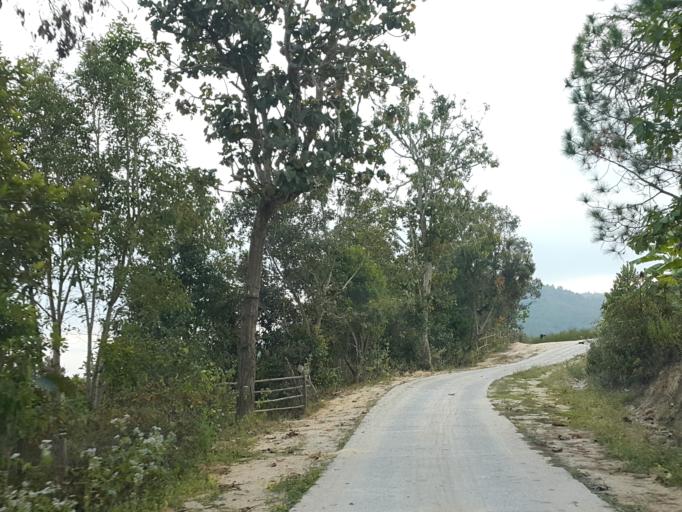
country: TH
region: Chiang Mai
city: Om Koi
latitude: 17.8059
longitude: 98.3190
